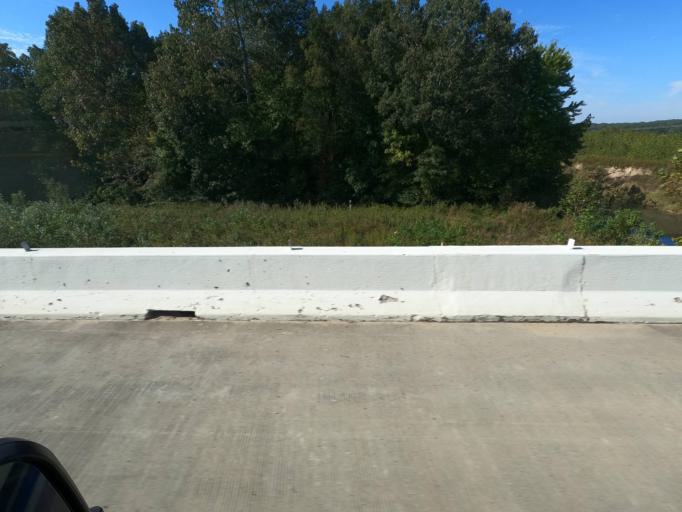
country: US
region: Tennessee
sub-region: Shelby County
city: Arlington
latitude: 35.2970
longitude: -89.6936
